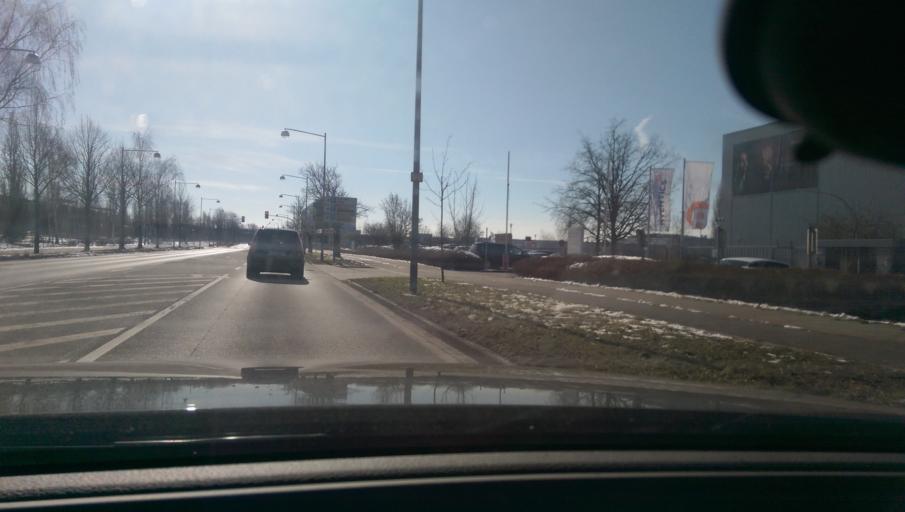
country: DE
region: Lower Saxony
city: Laatzen
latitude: 52.3227
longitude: 9.7950
